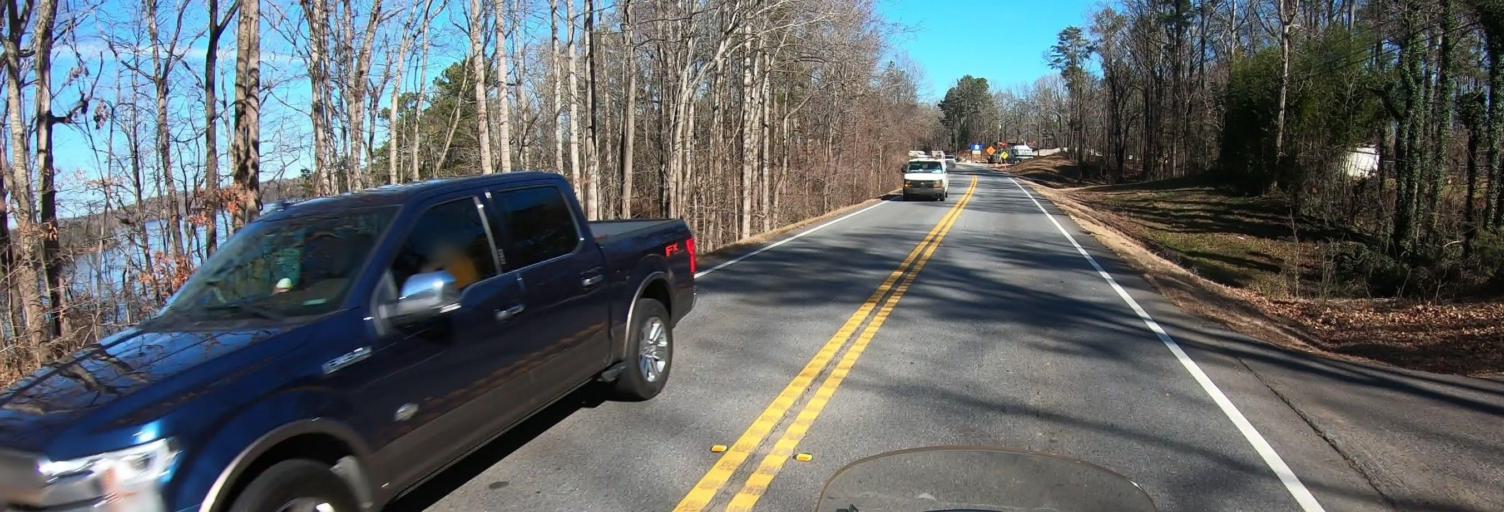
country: US
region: Georgia
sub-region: Hall County
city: Flowery Branch
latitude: 34.2586
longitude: -83.9617
